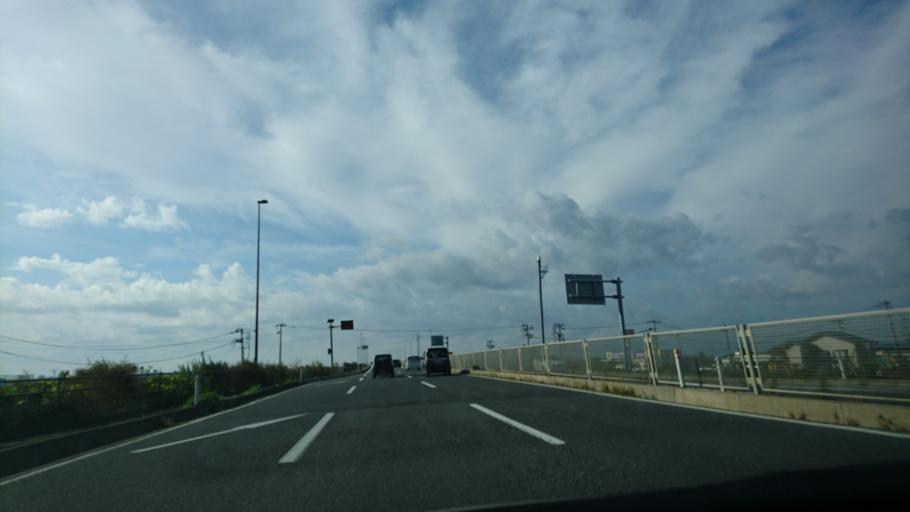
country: JP
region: Miyagi
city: Furukawa
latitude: 38.5973
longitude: 140.9679
